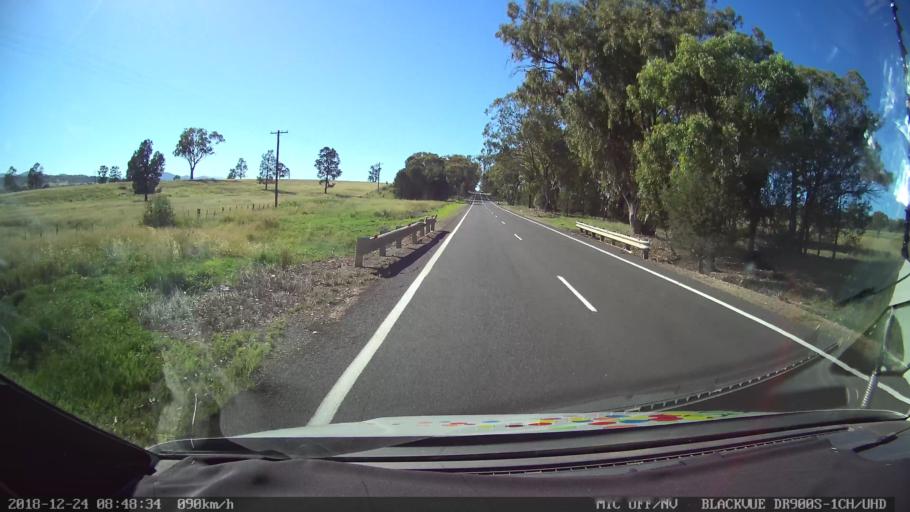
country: AU
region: New South Wales
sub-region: Liverpool Plains
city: Quirindi
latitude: -31.4574
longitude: 150.6467
